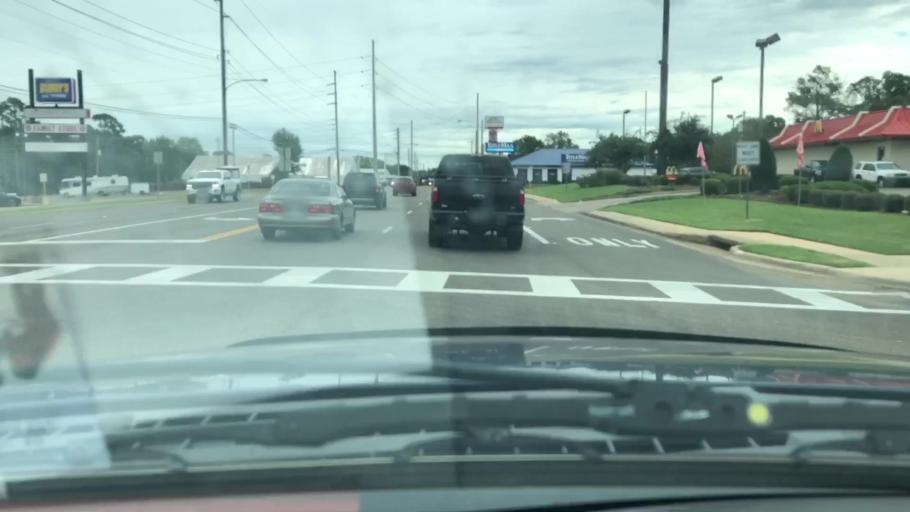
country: US
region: Texas
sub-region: Bowie County
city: Texarkana
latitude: 33.4349
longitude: -94.0628
